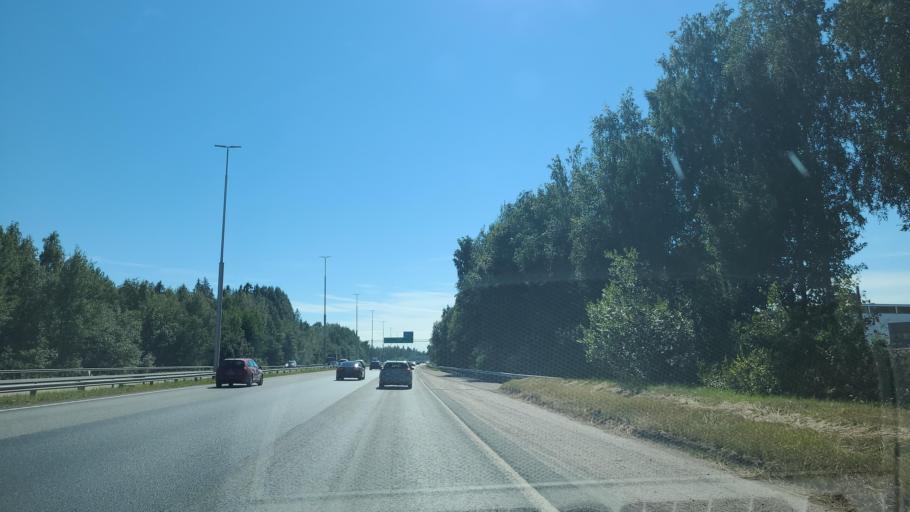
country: FI
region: Uusimaa
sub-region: Helsinki
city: Vantaa
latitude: 60.2466
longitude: 25.0557
